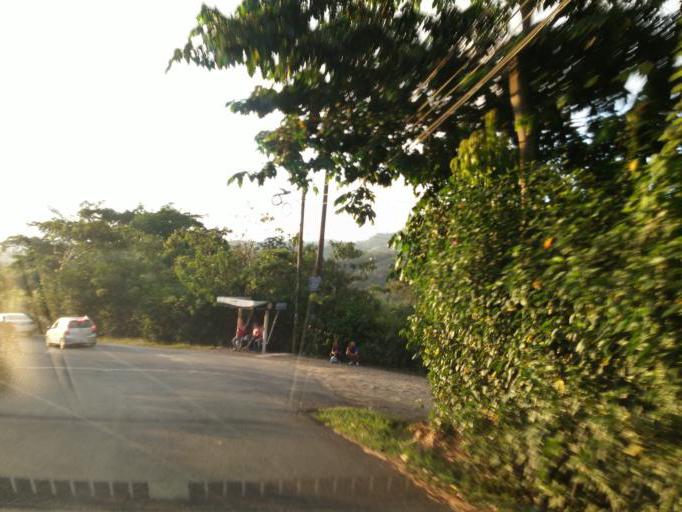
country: CR
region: San Jose
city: Palmichal
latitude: 9.8488
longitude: -84.2243
